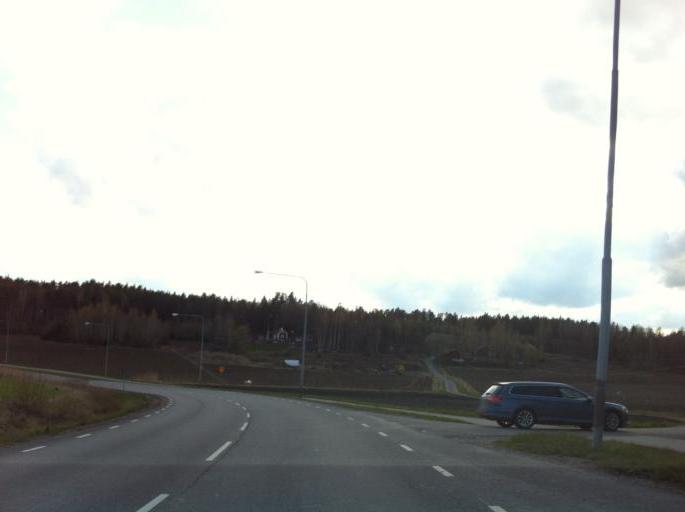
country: SE
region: Soedermanland
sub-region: Eskilstuna Kommun
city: Torshalla
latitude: 59.4308
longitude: 16.4545
